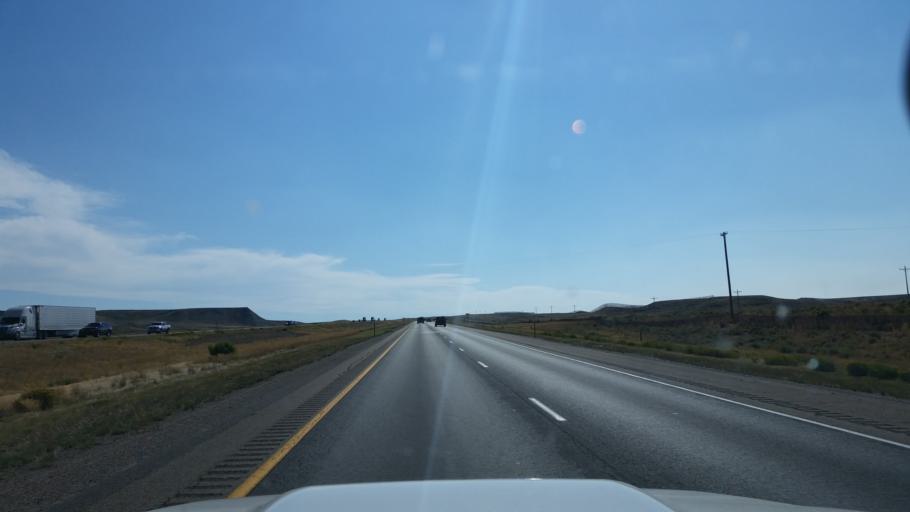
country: US
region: Wyoming
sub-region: Uinta County
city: Lyman
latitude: 41.5060
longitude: -109.9931
